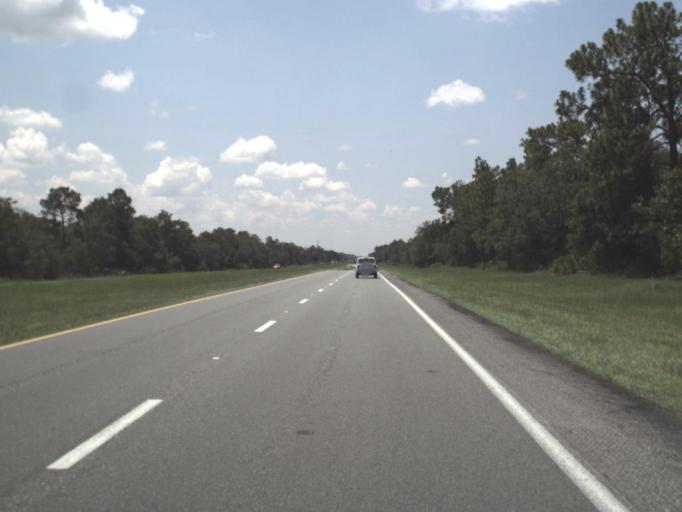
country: US
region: Florida
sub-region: Citrus County
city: Sugarmill Woods
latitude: 28.6499
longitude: -82.5523
